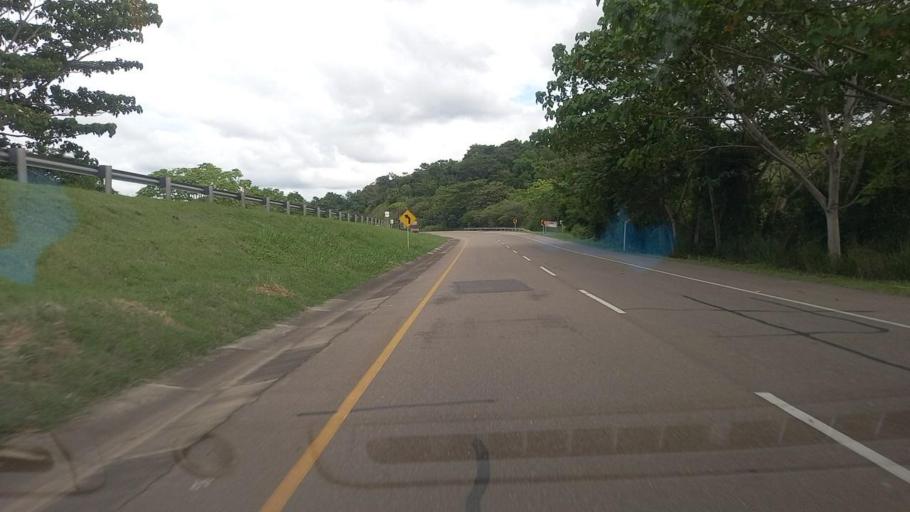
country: CO
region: Boyaca
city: Puerto Boyaca
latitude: 6.1521
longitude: -74.5714
